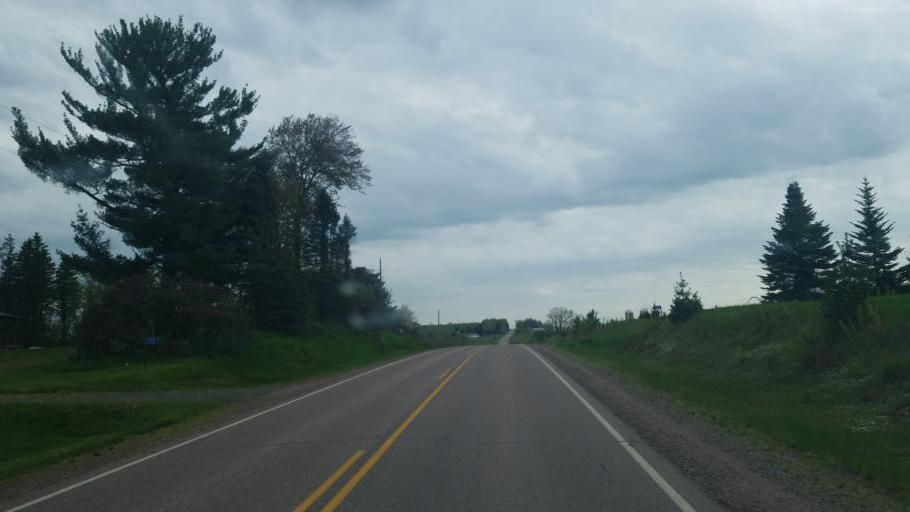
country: US
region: Wisconsin
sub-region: Wood County
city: Marshfield
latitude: 44.5784
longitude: -90.2996
